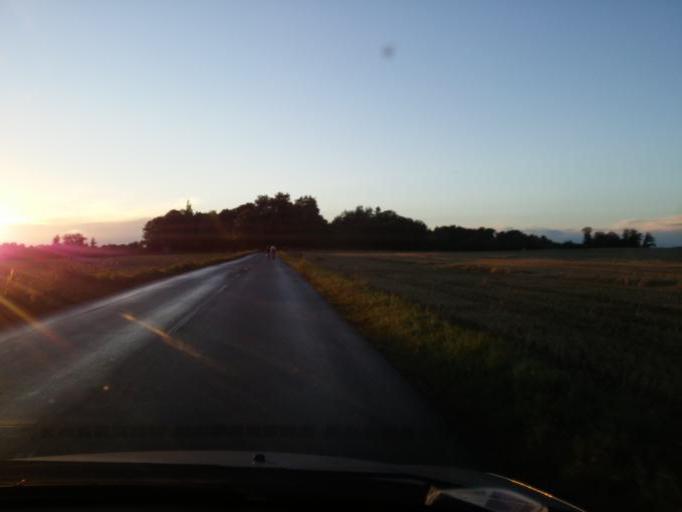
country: DK
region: South Denmark
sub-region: Kerteminde Kommune
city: Munkebo
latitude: 55.4245
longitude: 10.5427
